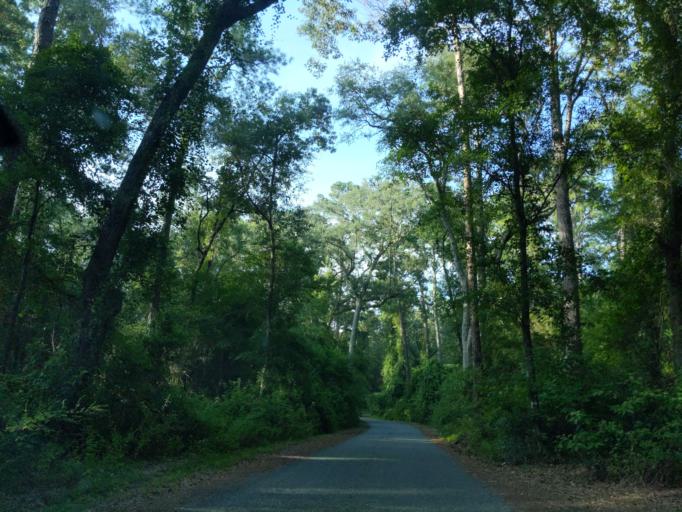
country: US
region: Florida
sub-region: Leon County
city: Tallahassee
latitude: 30.3496
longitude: -84.3638
